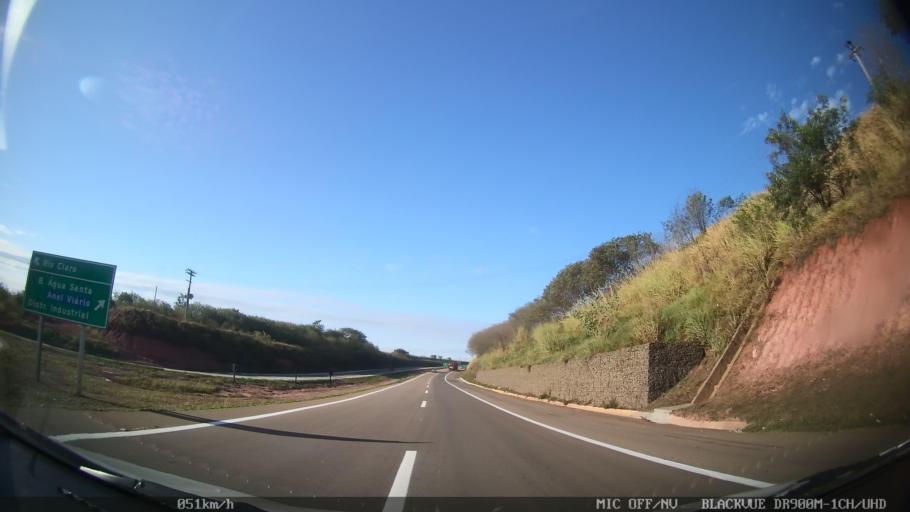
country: BR
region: Sao Paulo
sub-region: Piracicaba
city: Piracicaba
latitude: -22.6643
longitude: -47.6162
